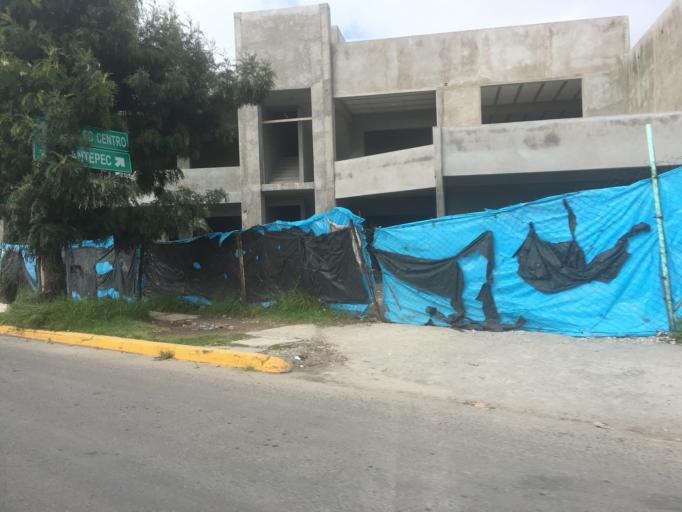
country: MX
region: Morelos
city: Metepec
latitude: 19.2787
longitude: -99.6080
